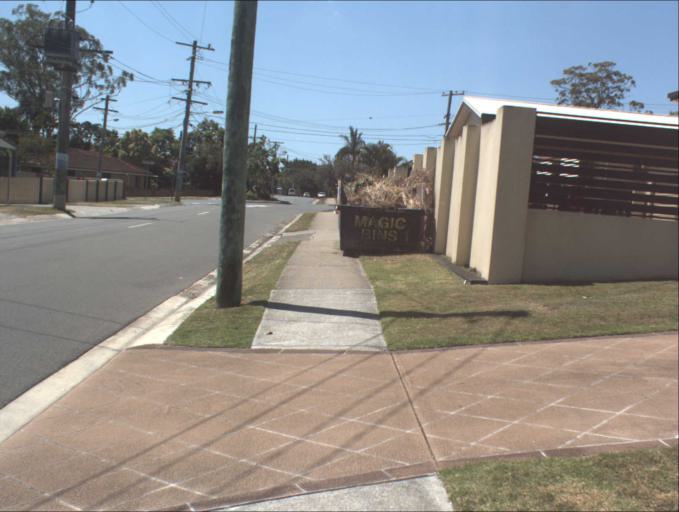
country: AU
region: Queensland
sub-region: Logan
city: Rochedale South
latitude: -27.5986
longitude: 153.1273
